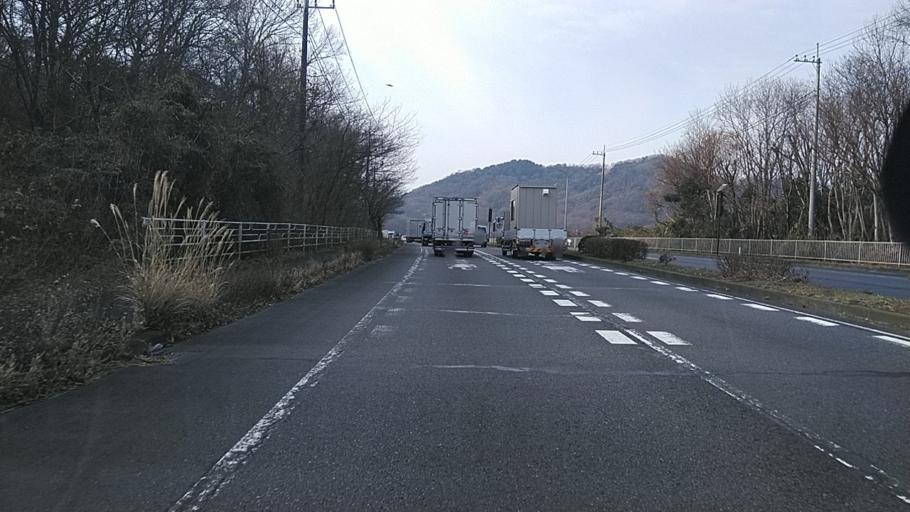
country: JP
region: Tochigi
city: Sano
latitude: 36.3089
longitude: 139.6421
